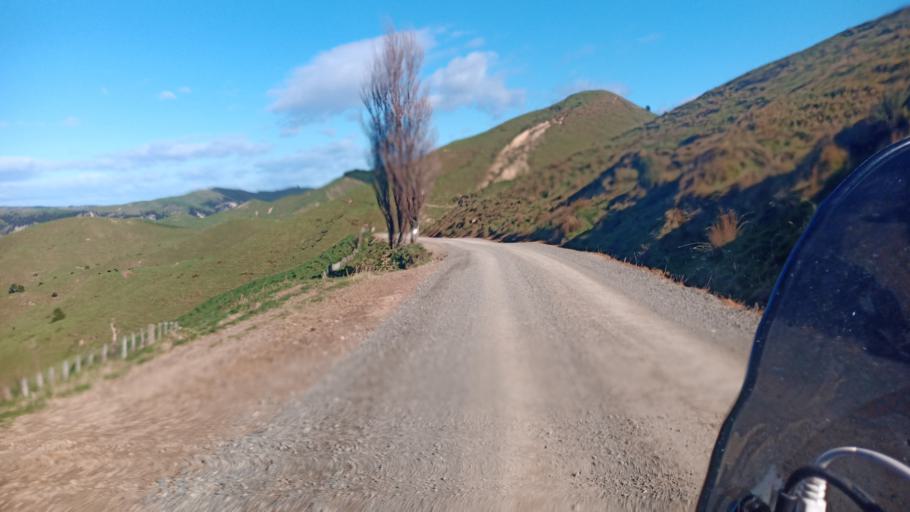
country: NZ
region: Hawke's Bay
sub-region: Wairoa District
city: Wairoa
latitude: -38.7807
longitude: 177.2665
